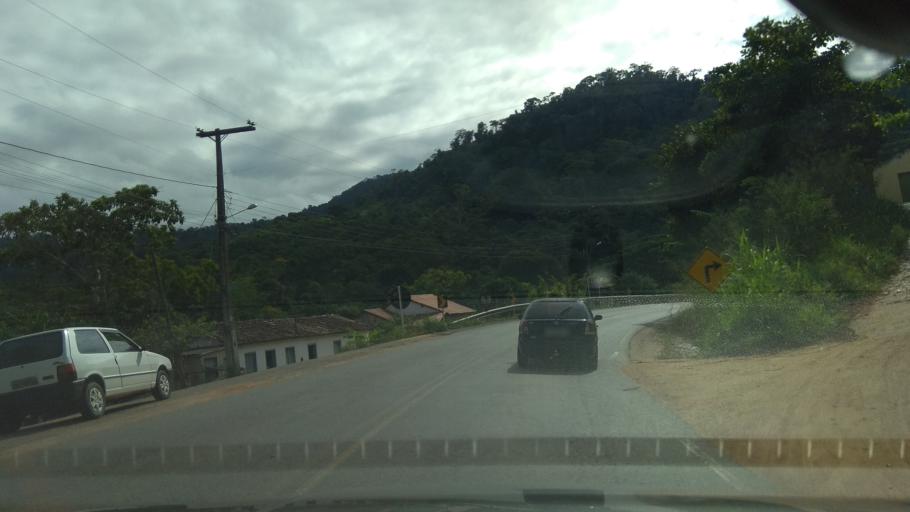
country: BR
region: Bahia
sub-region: Ubaira
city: Ubaira
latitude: -13.2584
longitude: -39.6175
